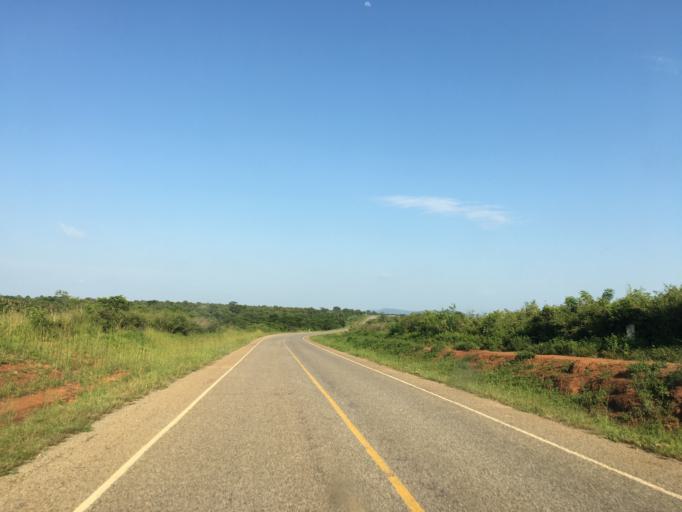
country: UG
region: Western Region
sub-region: Kiryandongo District
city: Masindi Port
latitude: 1.5851
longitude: 31.9134
